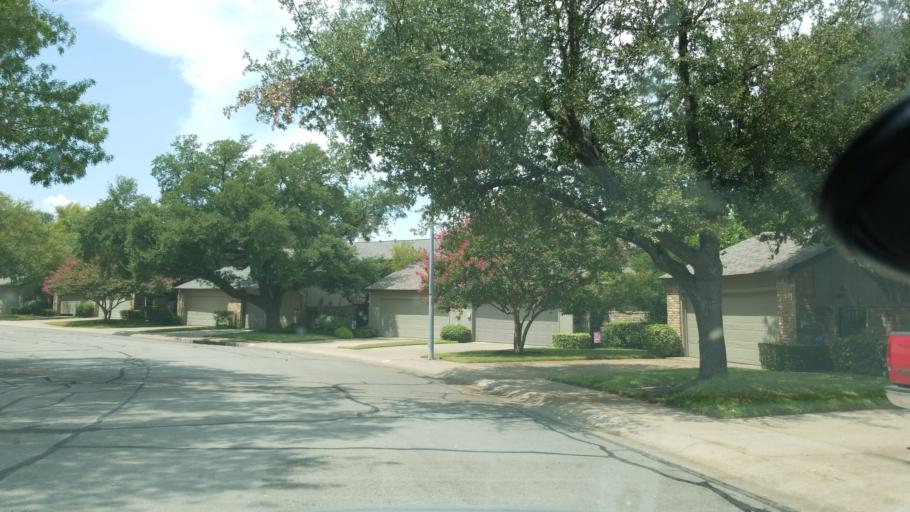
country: US
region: Texas
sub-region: Dallas County
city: Richardson
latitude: 32.8939
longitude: -96.7217
